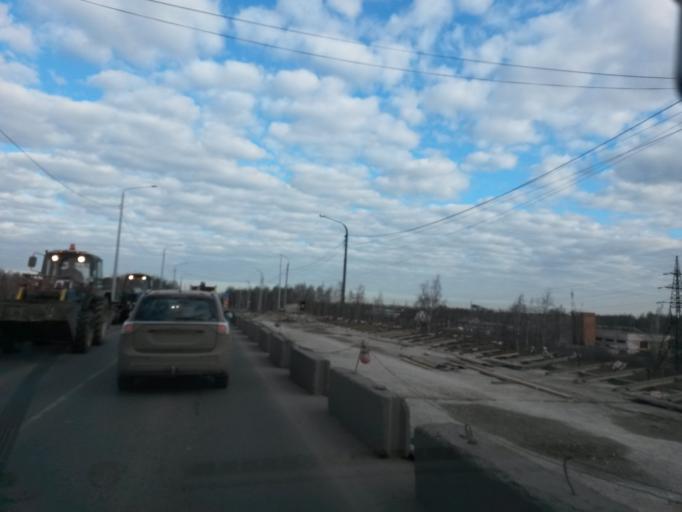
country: RU
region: Jaroslavl
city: Yaroslavl
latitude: 57.5883
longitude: 39.8192
